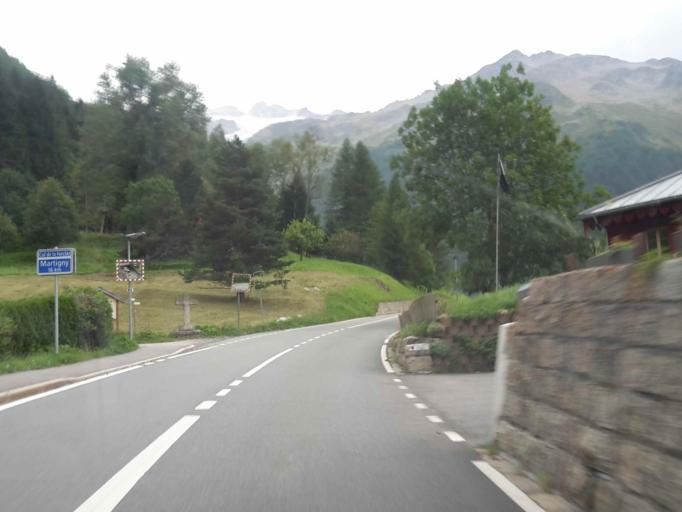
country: CH
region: Valais
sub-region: Martigny District
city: Martigny-Combe
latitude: 46.0551
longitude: 6.9963
